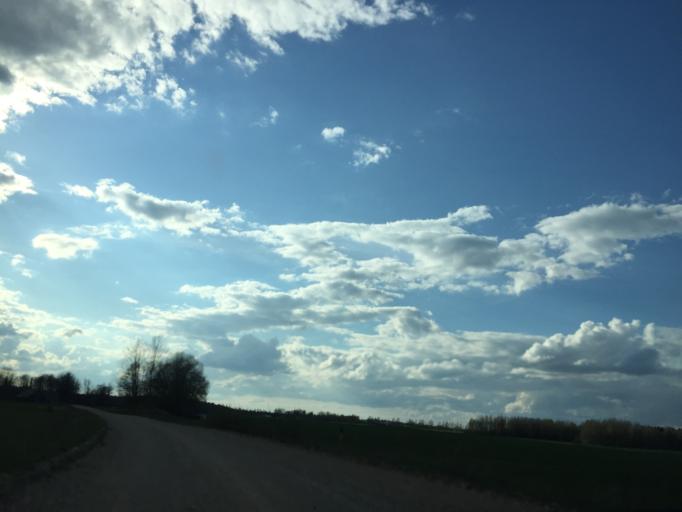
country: LV
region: Raunas
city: Rauna
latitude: 57.3696
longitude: 25.5072
